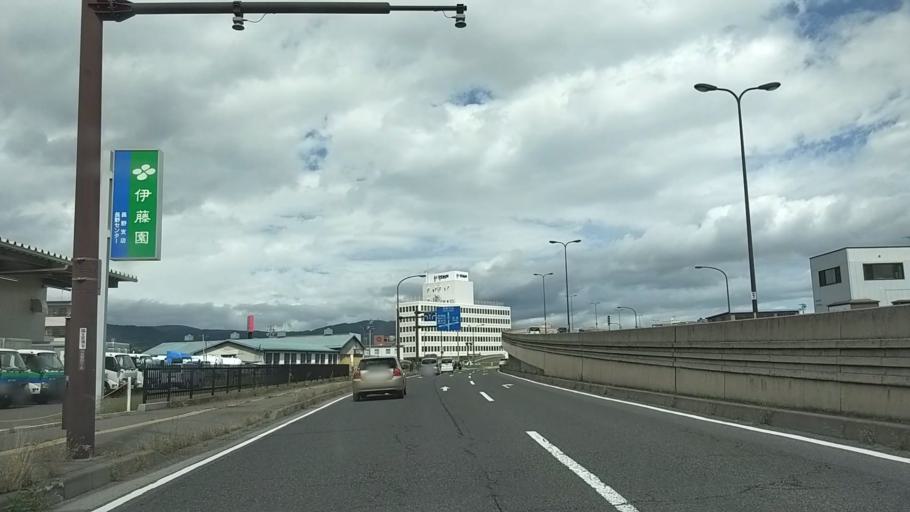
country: JP
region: Nagano
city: Nagano-shi
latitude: 36.6271
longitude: 138.2008
